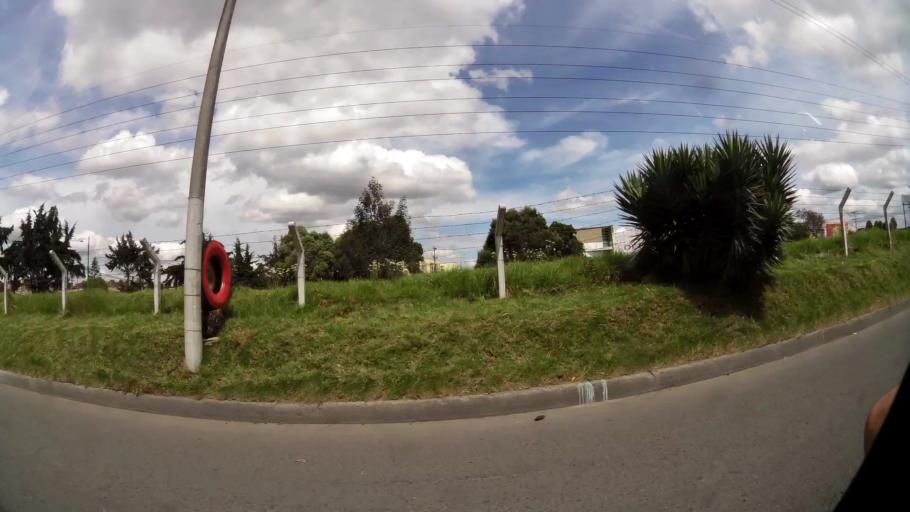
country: CO
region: Bogota D.C.
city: Bogota
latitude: 4.6994
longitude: -74.1143
